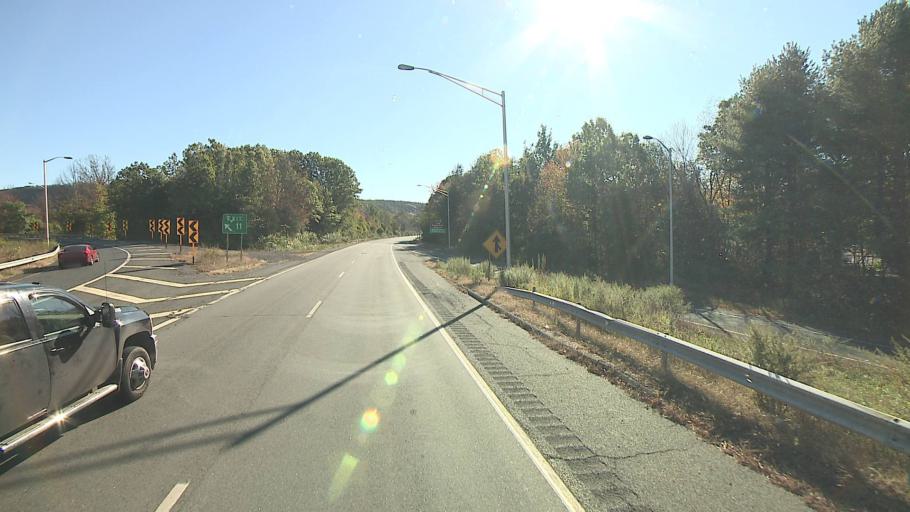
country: US
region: Connecticut
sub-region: New Haven County
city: Meriden
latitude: 41.5368
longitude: -72.7618
